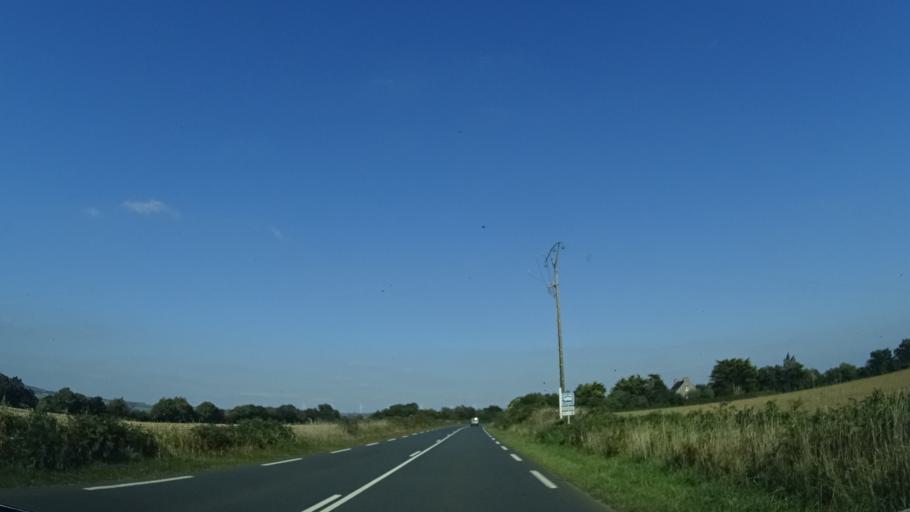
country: FR
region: Brittany
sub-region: Departement du Finistere
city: Cast
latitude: 48.1366
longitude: -4.1835
